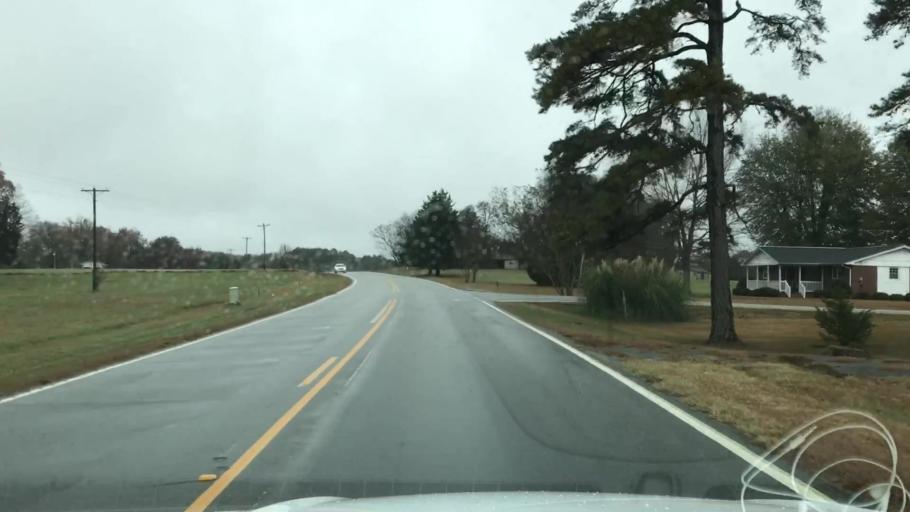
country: US
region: South Carolina
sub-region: Spartanburg County
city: Roebuck
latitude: 34.8276
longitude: -81.9235
